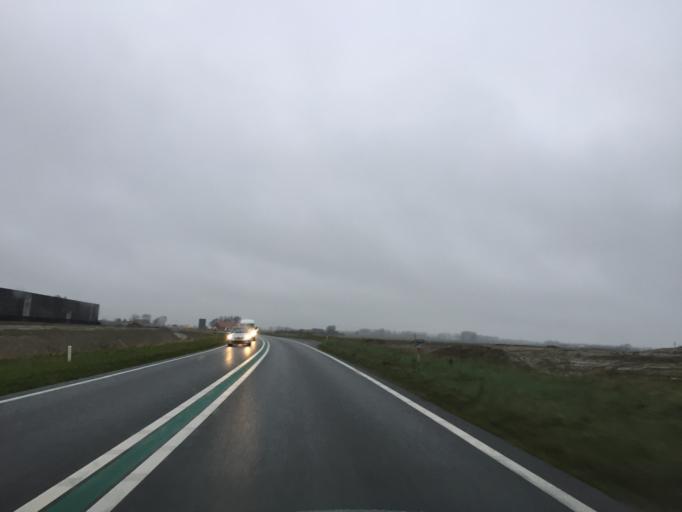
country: NL
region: Zeeland
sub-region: Gemeente Borsele
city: Borssele
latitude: 51.4641
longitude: 3.7637
